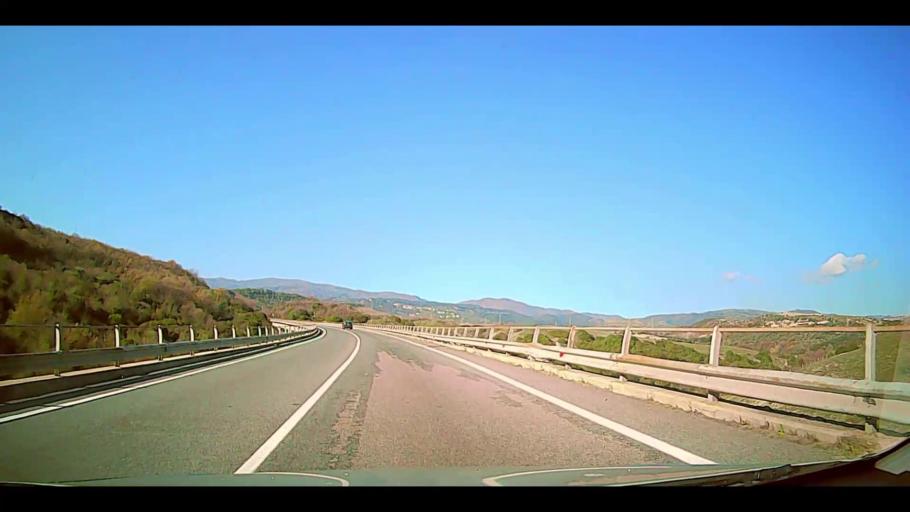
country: IT
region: Calabria
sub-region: Provincia di Crotone
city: Cotronei
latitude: 39.1874
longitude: 16.8279
